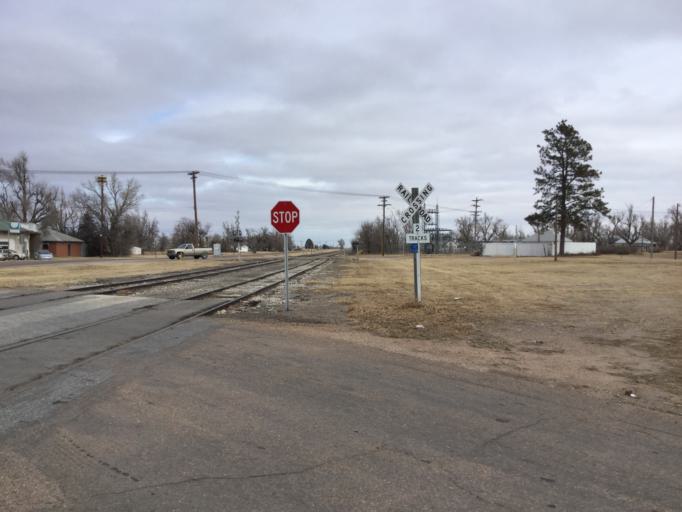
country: US
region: Kansas
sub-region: Pawnee County
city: Larned
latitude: 38.1811
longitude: -99.0930
